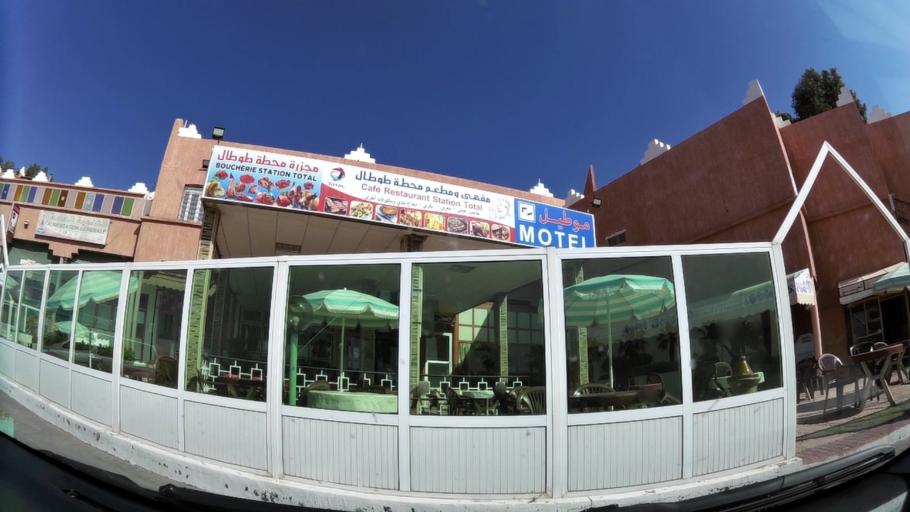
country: MA
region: Souss-Massa-Draa
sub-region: Inezgane-Ait Mellou
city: Inezgane
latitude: 30.3957
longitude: -9.4610
